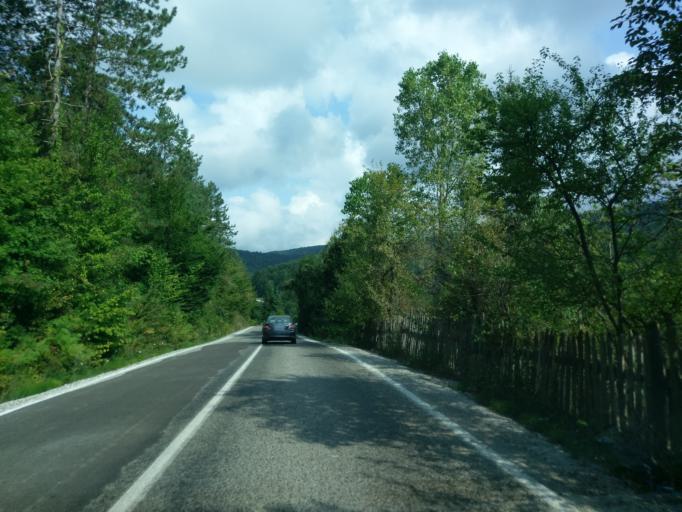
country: TR
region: Sinop
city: Ayancik
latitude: 41.8823
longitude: 34.5201
